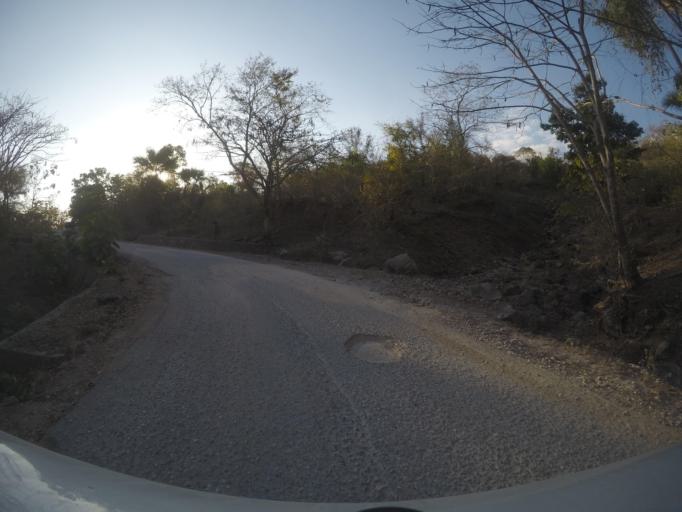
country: ID
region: East Nusa Tenggara
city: Atambua
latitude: -8.9637
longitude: 125.0246
